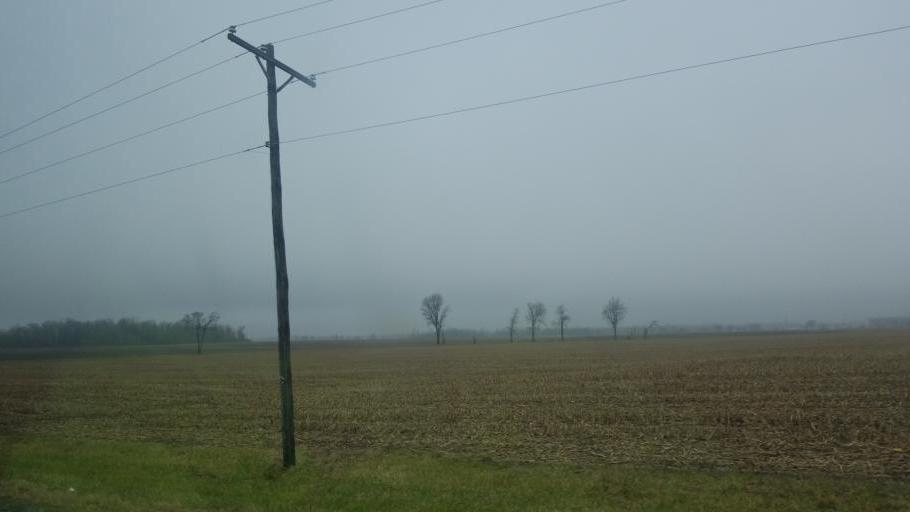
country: US
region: Ohio
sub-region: Champaign County
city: North Lewisburg
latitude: 40.2376
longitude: -83.5660
